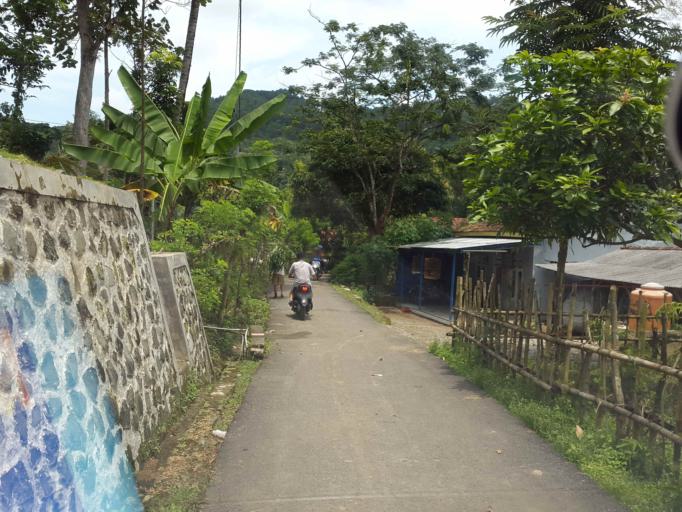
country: ID
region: Central Java
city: Muara
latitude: -7.2592
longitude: 108.8850
